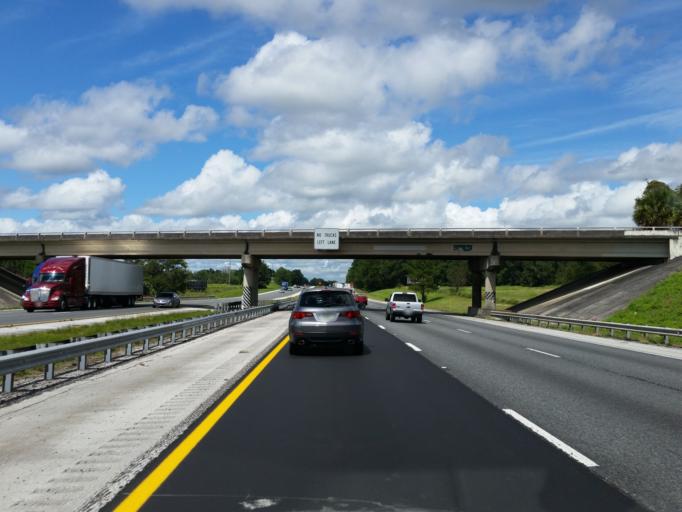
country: US
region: Florida
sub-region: Marion County
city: Ocala
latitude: 29.2956
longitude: -82.2034
